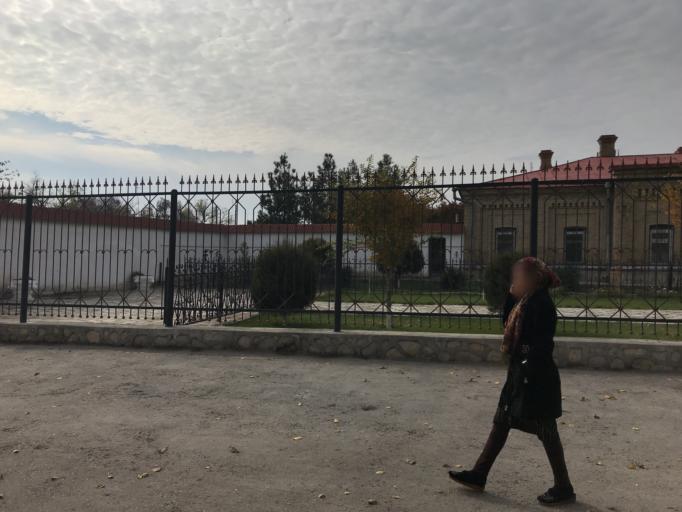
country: UZ
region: Bukhara
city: Kogon
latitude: 39.7194
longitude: 64.5488
